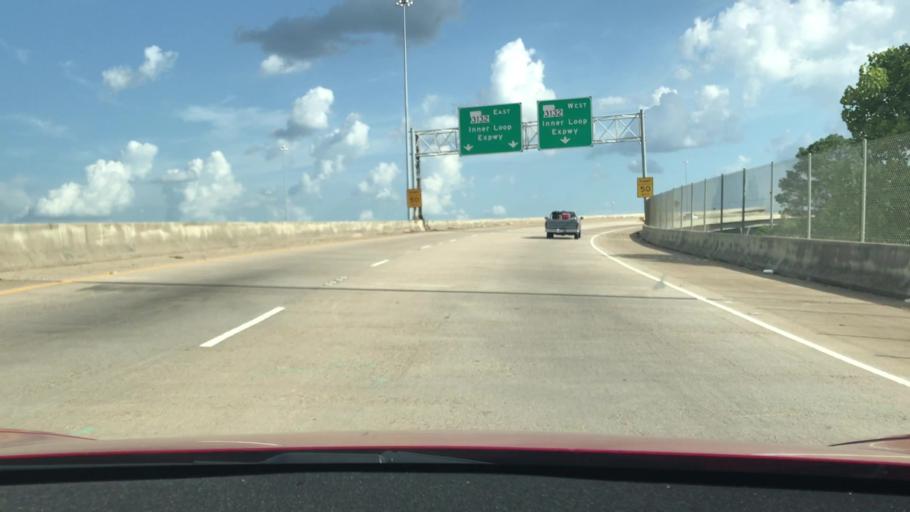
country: US
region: Louisiana
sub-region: Bossier Parish
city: Bossier City
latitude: 32.4235
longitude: -93.7501
